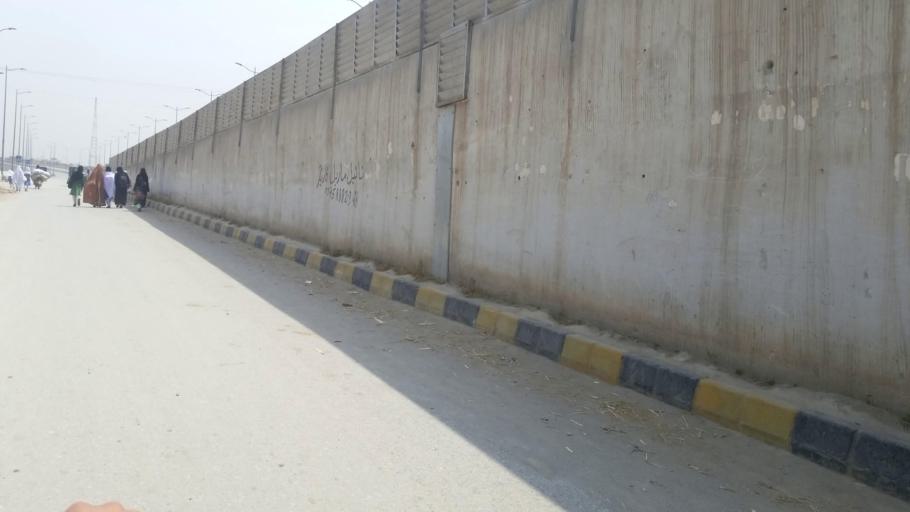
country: PK
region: Khyber Pakhtunkhwa
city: Peshawar
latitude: 34.0300
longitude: 71.5481
